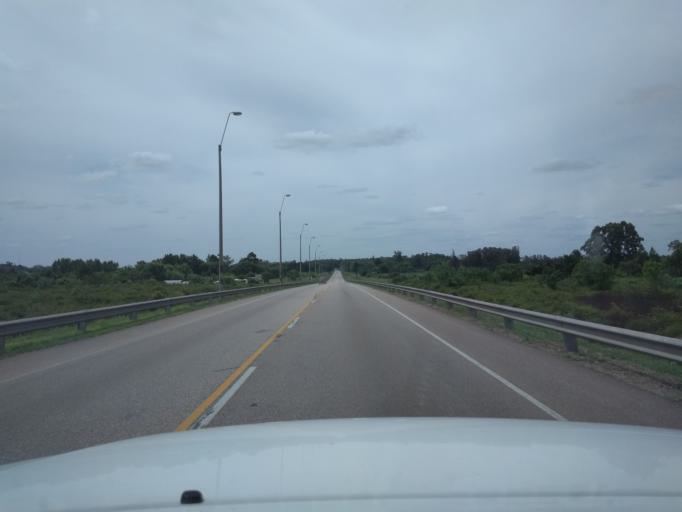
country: UY
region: Canelones
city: Canelones
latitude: -34.5424
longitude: -56.2742
